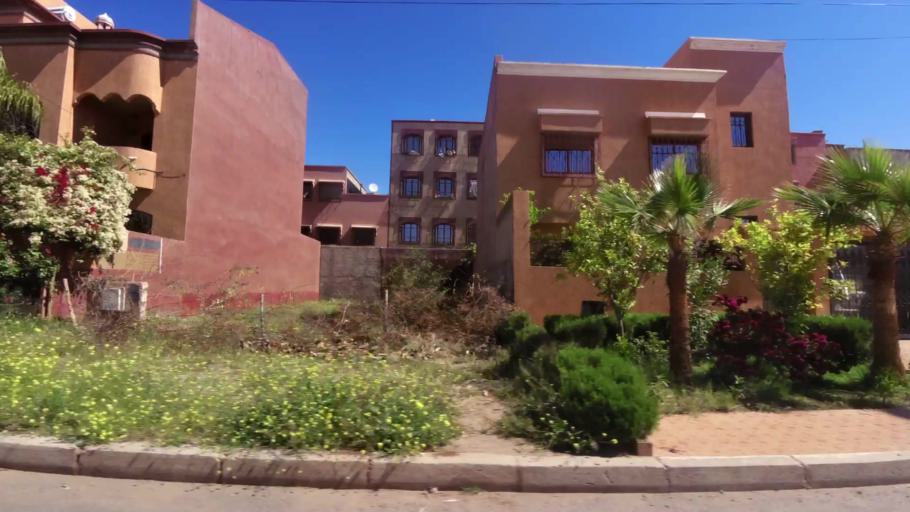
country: MA
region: Marrakech-Tensift-Al Haouz
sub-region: Marrakech
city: Marrakesh
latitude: 31.5709
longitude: -8.0605
